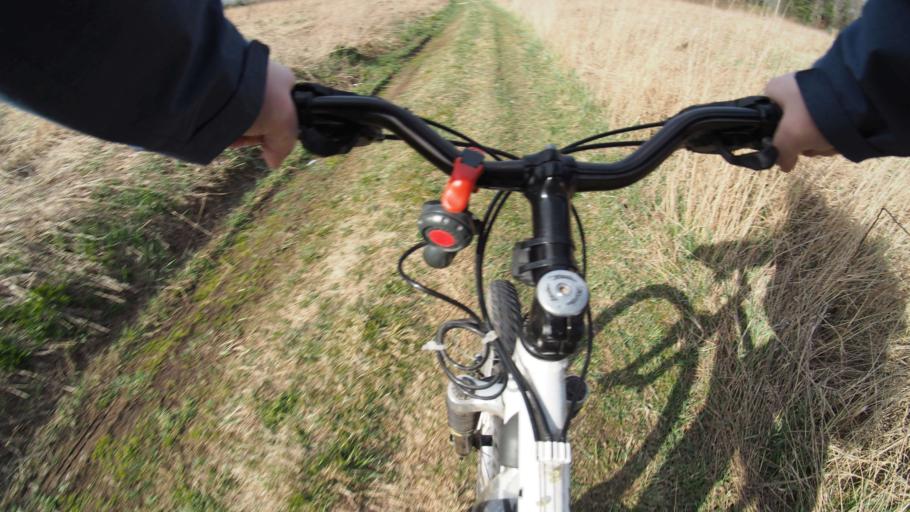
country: RU
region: Moskovskaya
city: Ramenskoye
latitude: 55.5995
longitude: 38.2886
